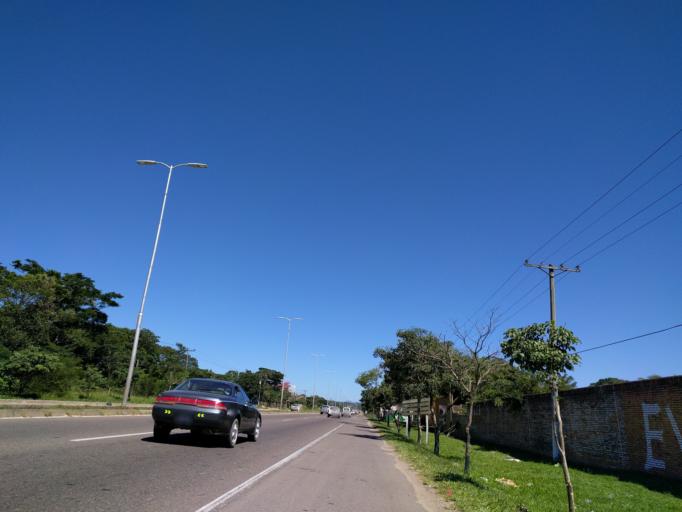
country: BO
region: Santa Cruz
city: Santa Rita
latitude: -17.8720
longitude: -63.2763
